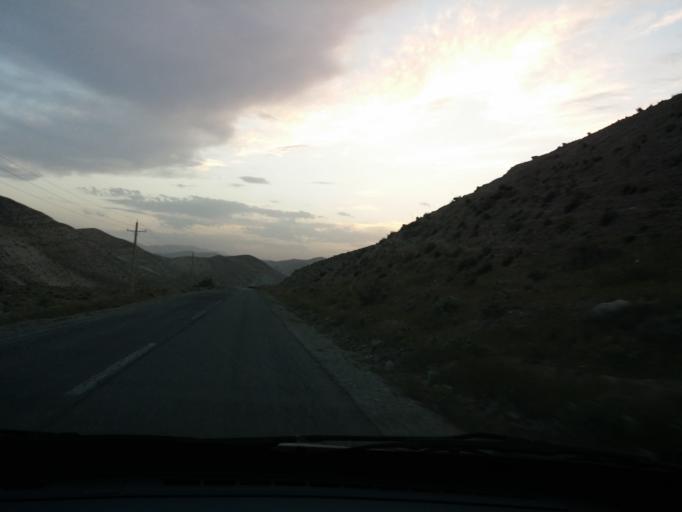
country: IR
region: Tehran
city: Damavand
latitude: 35.5452
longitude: 52.2798
